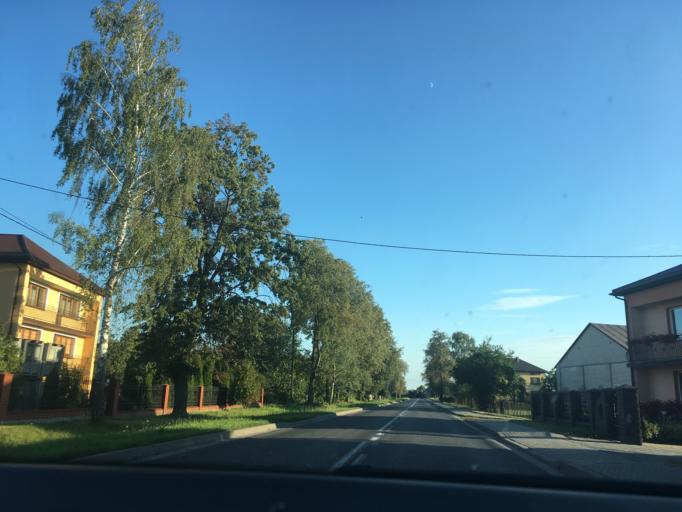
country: PL
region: Masovian Voivodeship
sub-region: Powiat losicki
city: Losice
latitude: 52.1527
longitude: 22.7486
